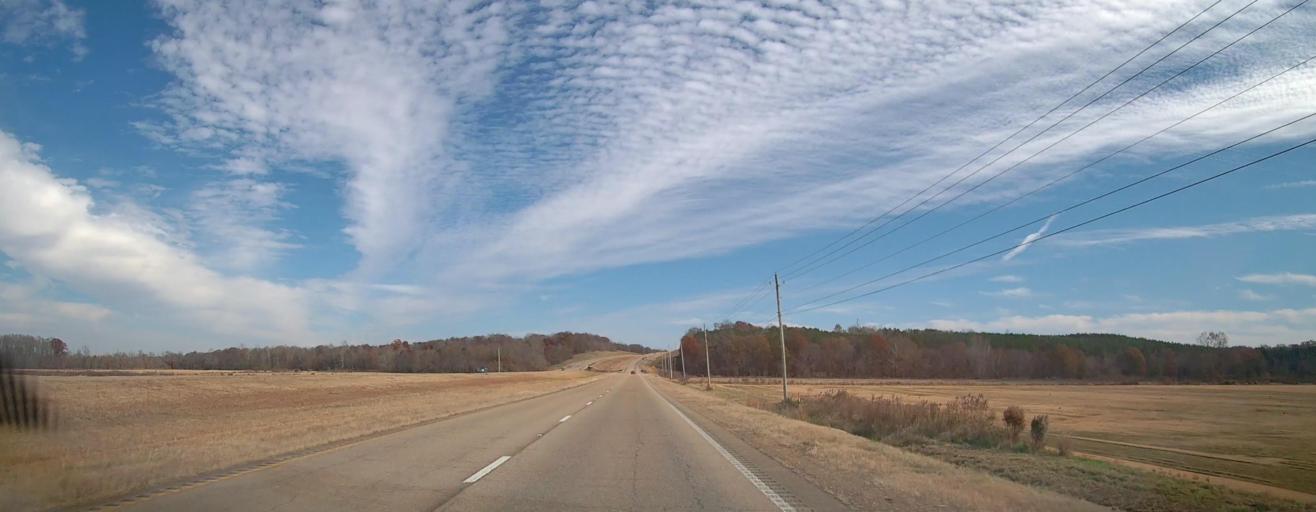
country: US
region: Mississippi
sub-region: Alcorn County
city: Corinth
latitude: 34.9319
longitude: -88.6578
